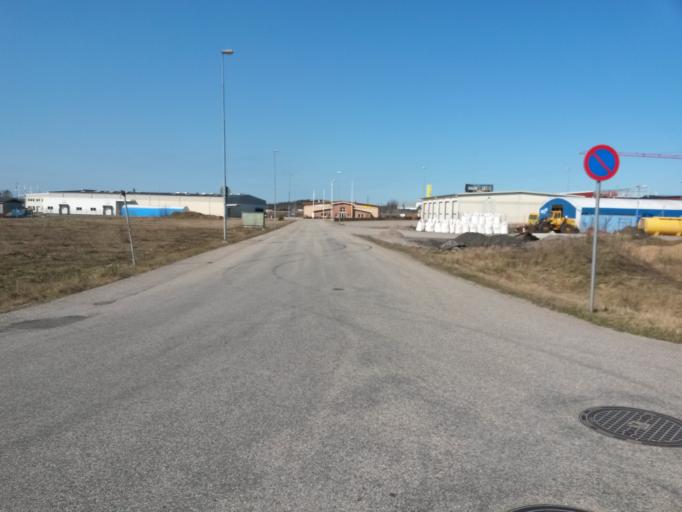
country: SE
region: Vaestra Goetaland
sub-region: Vargarda Kommun
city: Vargarda
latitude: 58.0414
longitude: 12.8053
